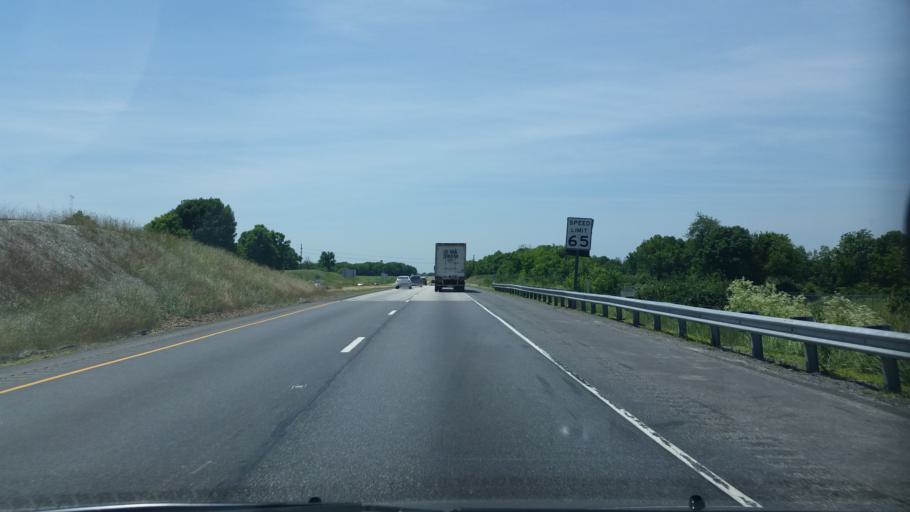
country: US
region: Pennsylvania
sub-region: Franklin County
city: Greencastle
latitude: 39.7765
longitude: -77.7175
